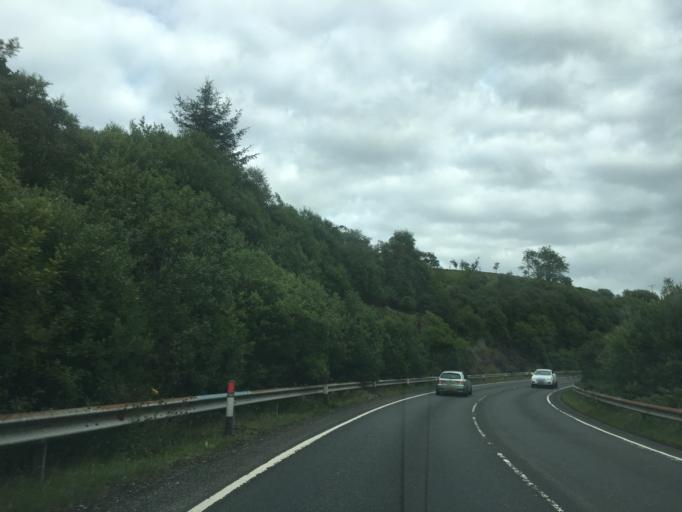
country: GB
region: Scotland
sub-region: Argyll and Bute
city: Oban
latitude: 56.3121
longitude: -5.4712
